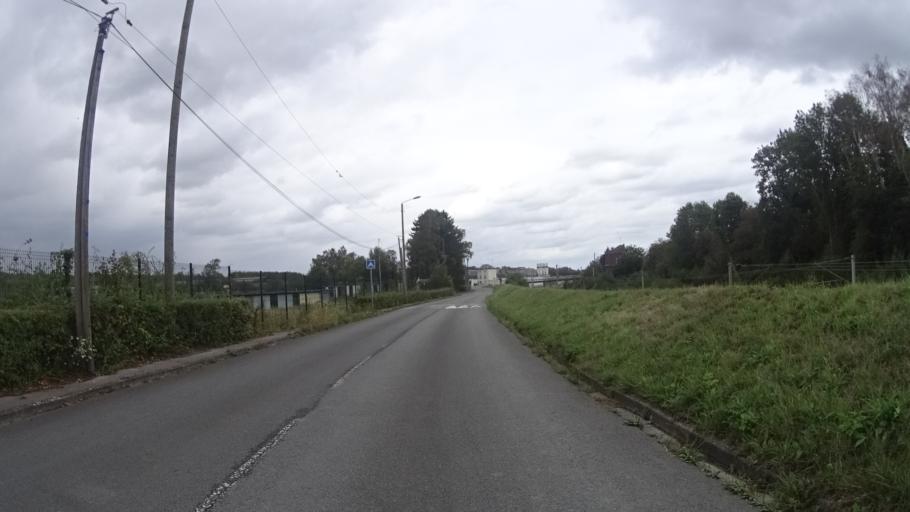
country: FR
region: Nord-Pas-de-Calais
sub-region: Departement du Nord
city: Hautmont
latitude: 50.2418
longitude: 3.8961
